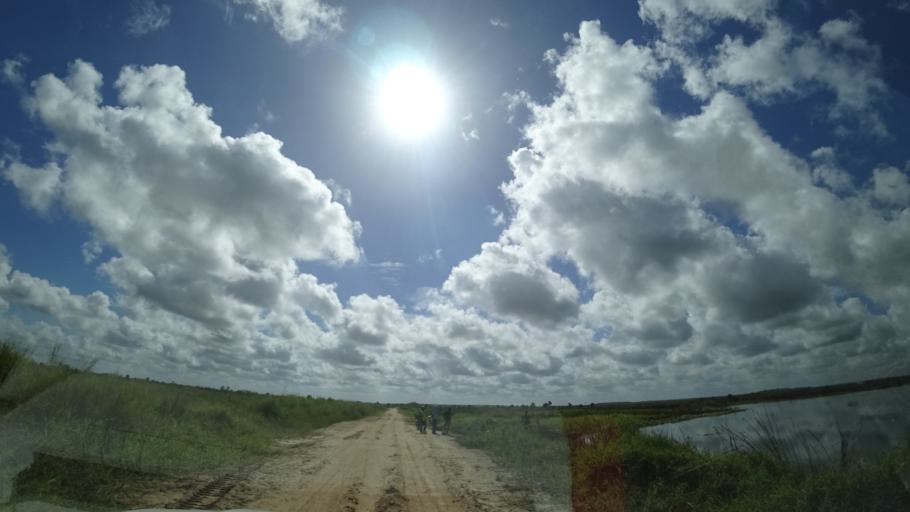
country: MZ
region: Sofala
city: Dondo
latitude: -19.3948
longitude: 34.5733
